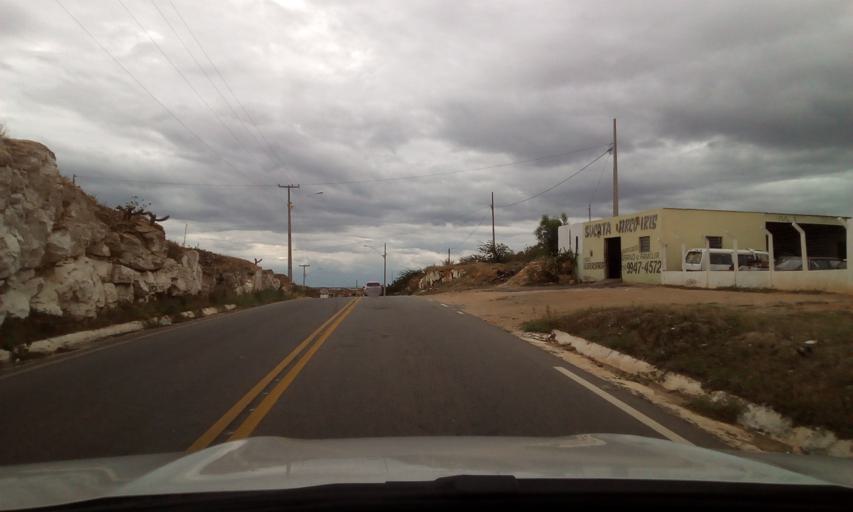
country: BR
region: Paraiba
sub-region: Picui
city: Picui
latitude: -6.5163
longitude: -36.3338
